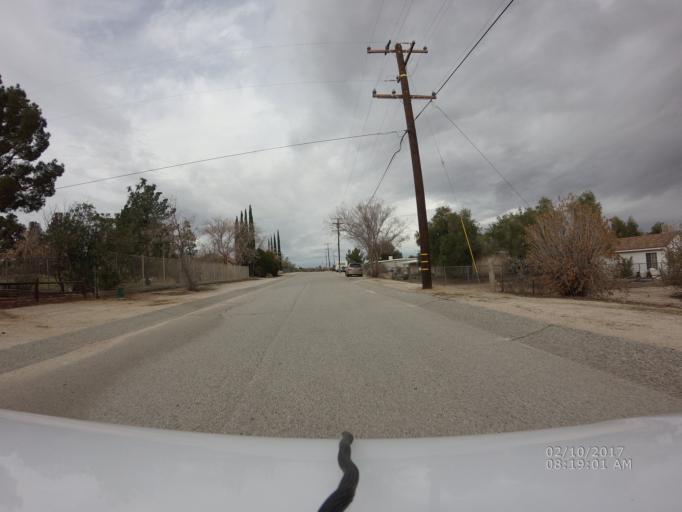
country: US
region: California
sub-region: Los Angeles County
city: Littlerock
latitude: 34.5047
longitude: -117.9127
